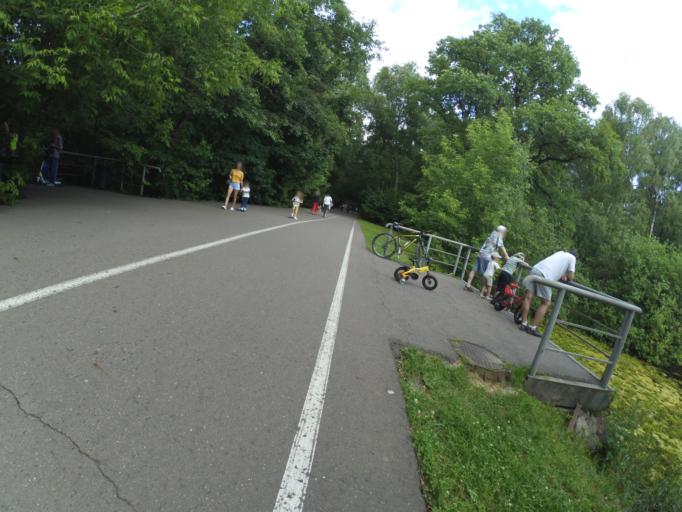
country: RU
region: Moscow
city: Ostankinskiy
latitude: 55.8426
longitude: 37.6134
